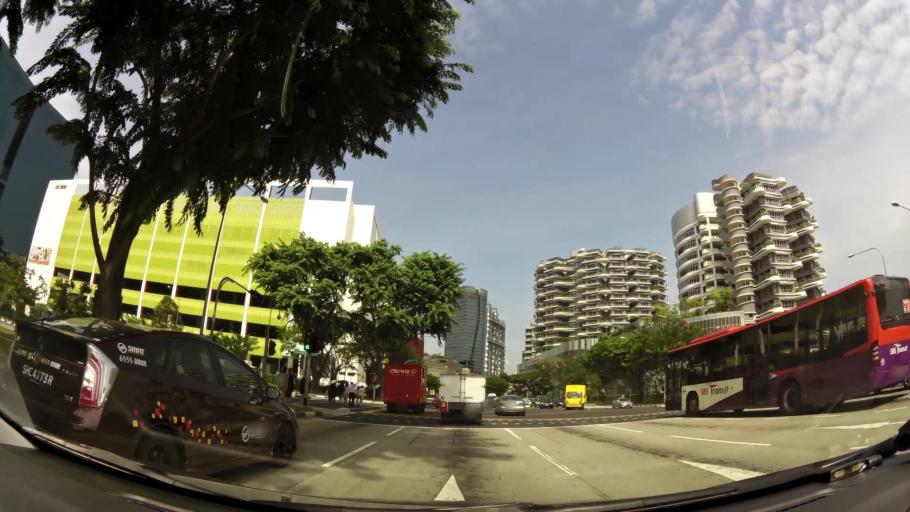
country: SG
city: Singapore
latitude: 1.3313
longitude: 103.7470
